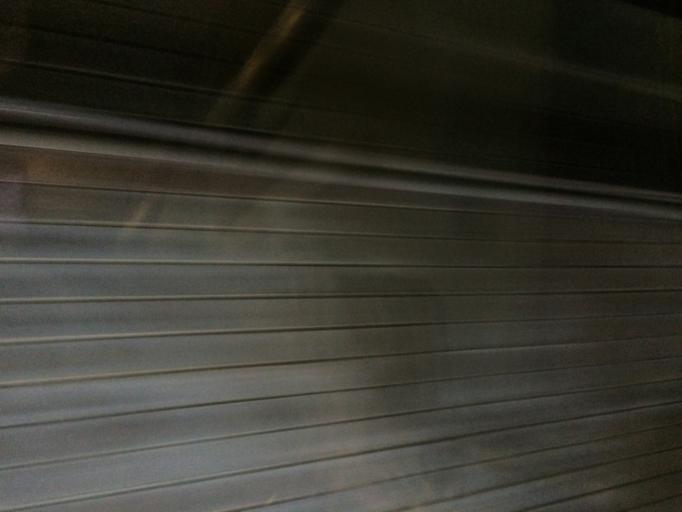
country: GB
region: Scotland
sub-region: Falkirk
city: Larbert
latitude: 56.0011
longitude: -3.8495
